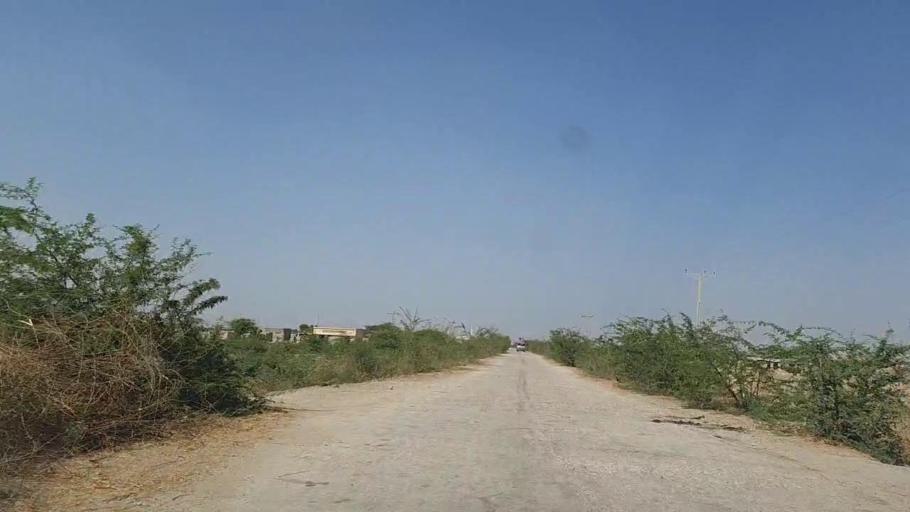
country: PK
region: Sindh
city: Naukot
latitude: 24.6356
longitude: 69.2882
